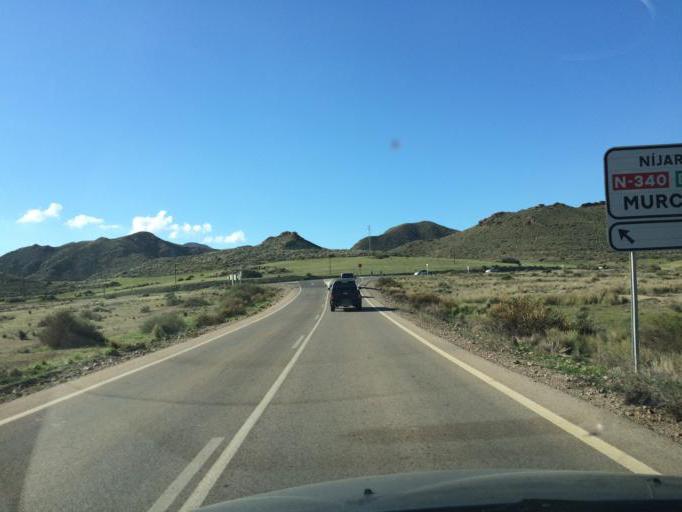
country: ES
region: Andalusia
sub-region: Provincia de Almeria
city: San Jose
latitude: 36.7948
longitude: -2.1122
